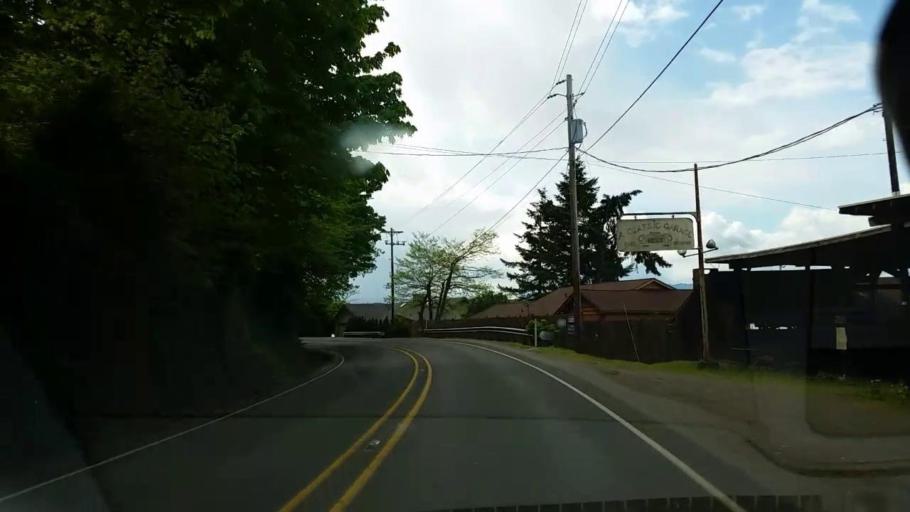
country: US
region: Washington
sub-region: Mason County
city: Shelton
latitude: 47.3572
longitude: -123.1037
